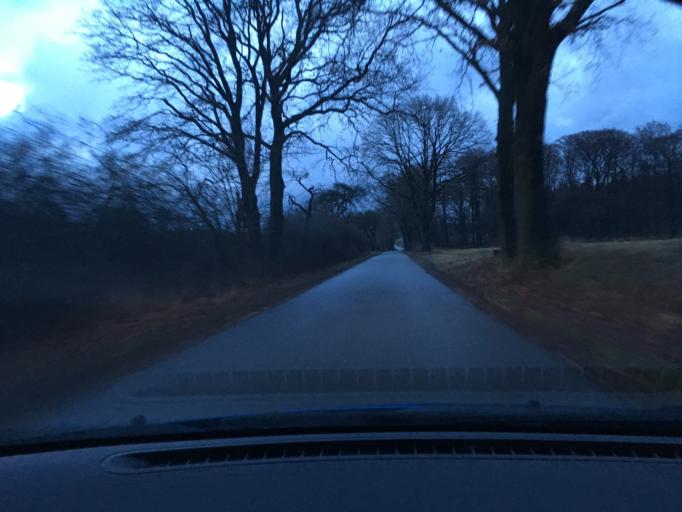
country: DE
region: Lower Saxony
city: Betzendorf
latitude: 53.1449
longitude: 10.3199
